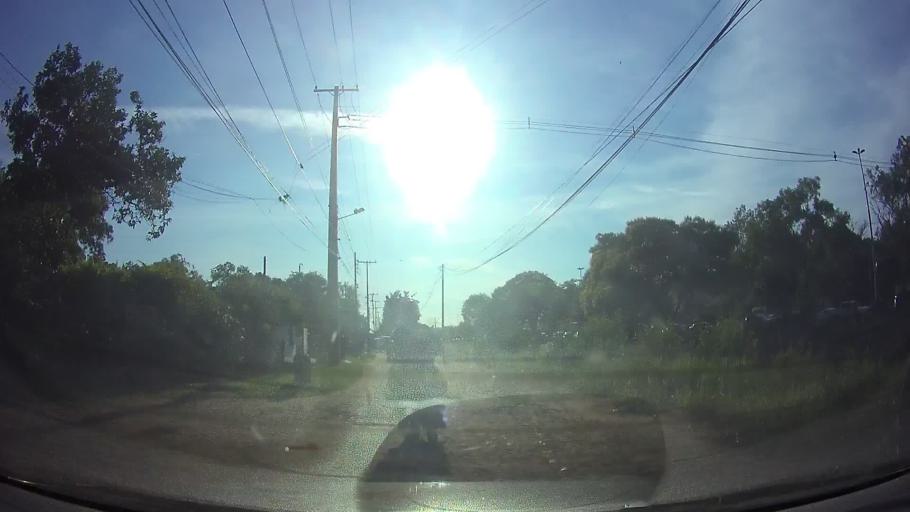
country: PY
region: Central
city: Fernando de la Mora
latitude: -25.2637
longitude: -57.5096
